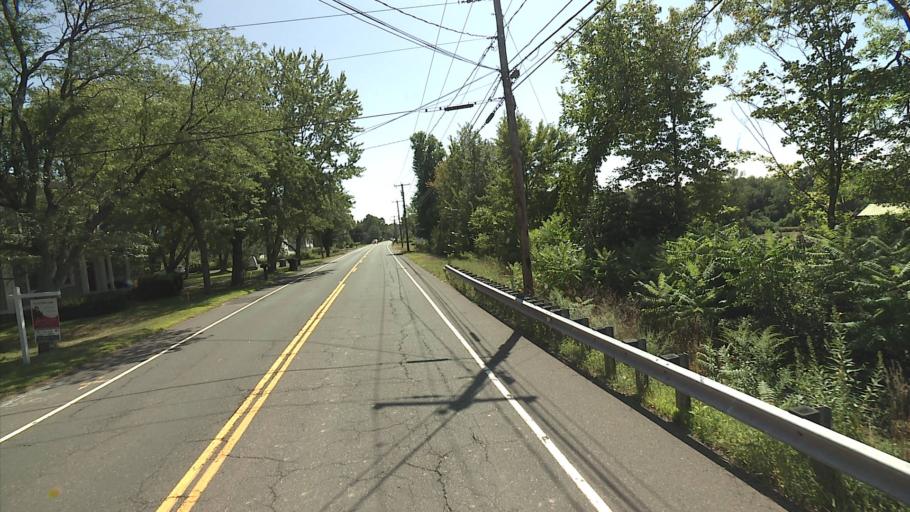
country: US
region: Connecticut
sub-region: Hartford County
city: Windsor Locks
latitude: 41.9540
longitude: -72.6276
